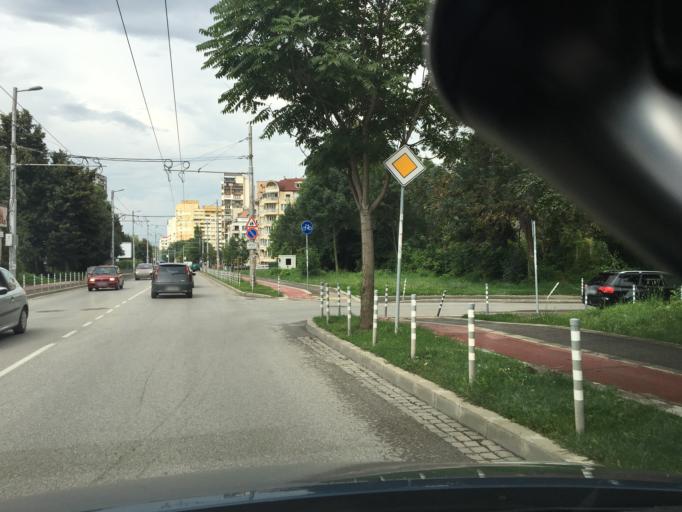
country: BG
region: Sofia-Capital
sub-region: Stolichna Obshtina
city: Sofia
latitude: 42.6658
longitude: 23.2755
